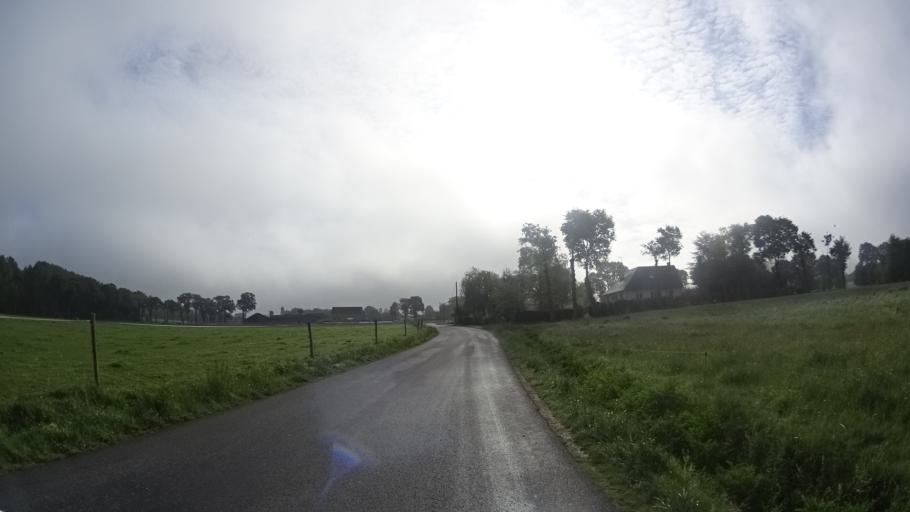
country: FR
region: Brittany
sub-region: Departement d'Ille-et-Vilaine
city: Mordelles
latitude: 48.0836
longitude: -1.8495
